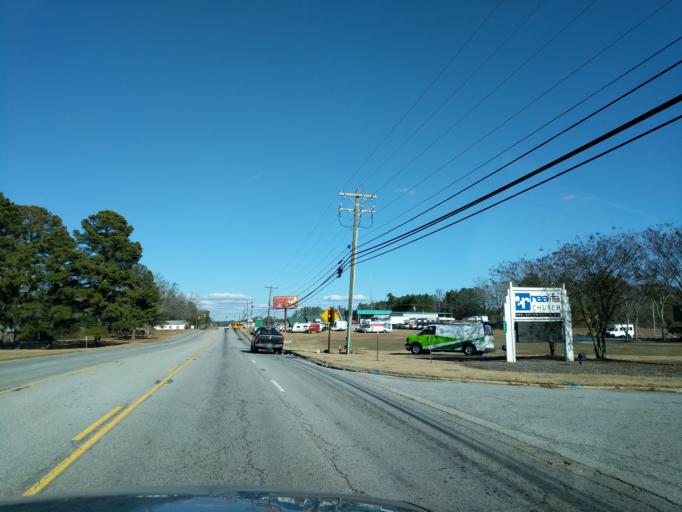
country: US
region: South Carolina
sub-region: Greenwood County
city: Greenwood
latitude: 34.2211
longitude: -82.1217
